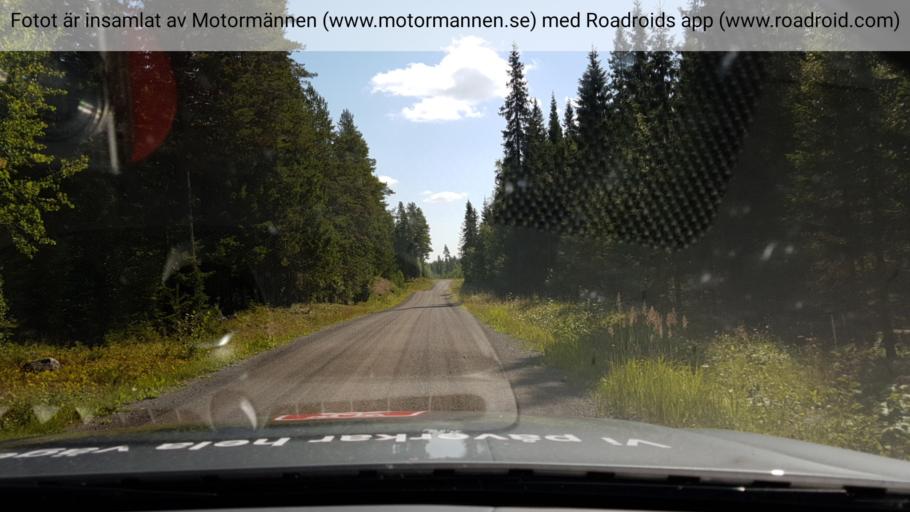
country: SE
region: Jaemtland
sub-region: OEstersunds Kommun
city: Lit
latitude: 63.3487
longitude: 15.2576
